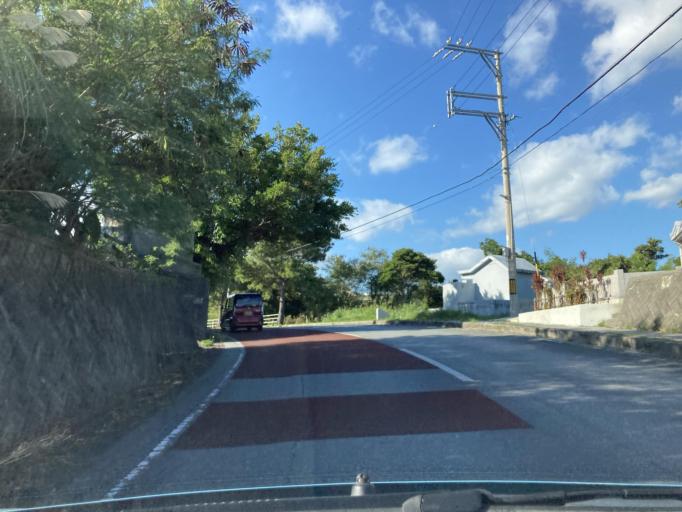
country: JP
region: Okinawa
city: Ginowan
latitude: 26.2170
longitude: 127.7513
